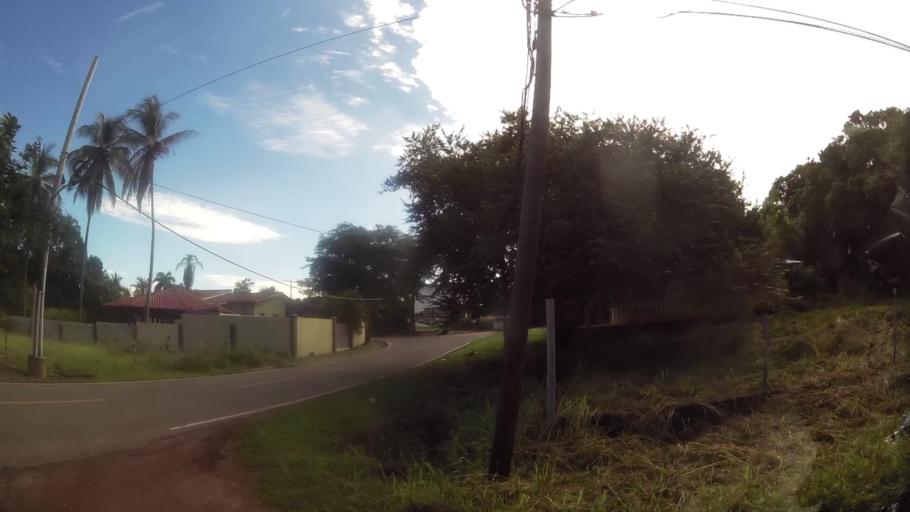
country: PA
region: Panama
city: Nueva Gorgona
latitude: 8.5326
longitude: -79.8795
